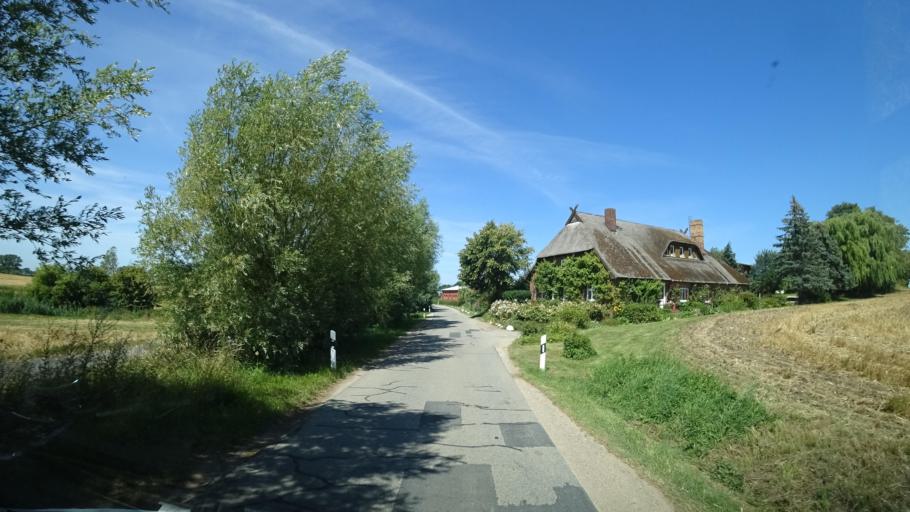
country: DE
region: Mecklenburg-Vorpommern
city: Blowatz
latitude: 54.0198
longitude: 11.5603
